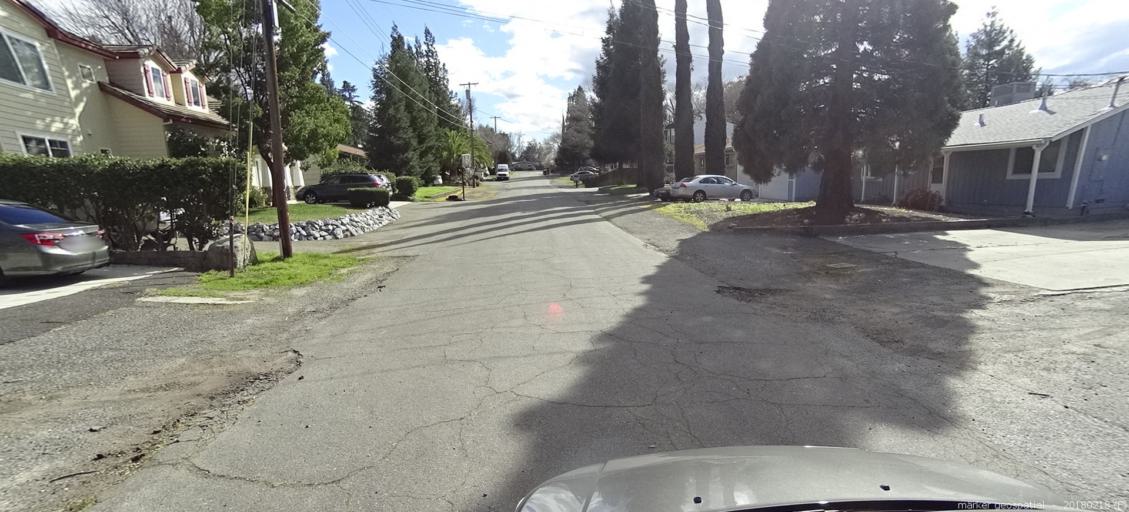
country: US
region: California
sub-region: Sacramento County
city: Orangevale
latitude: 38.7016
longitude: -121.2082
